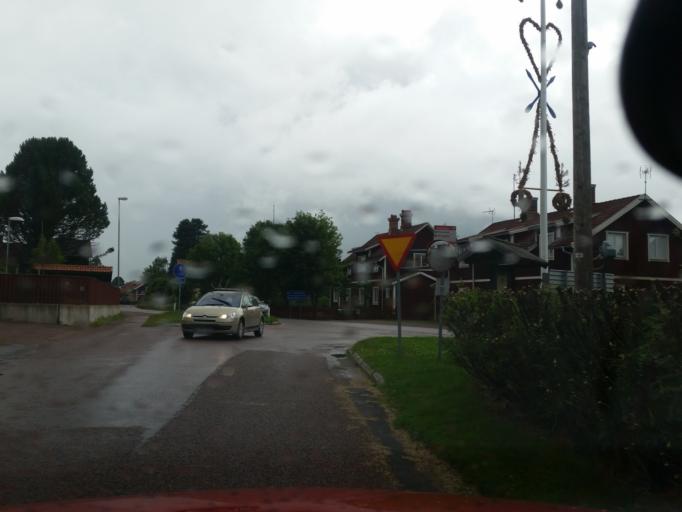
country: SE
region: Dalarna
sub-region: Leksand Municipality
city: Smedby
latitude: 60.6997
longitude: 15.0486
